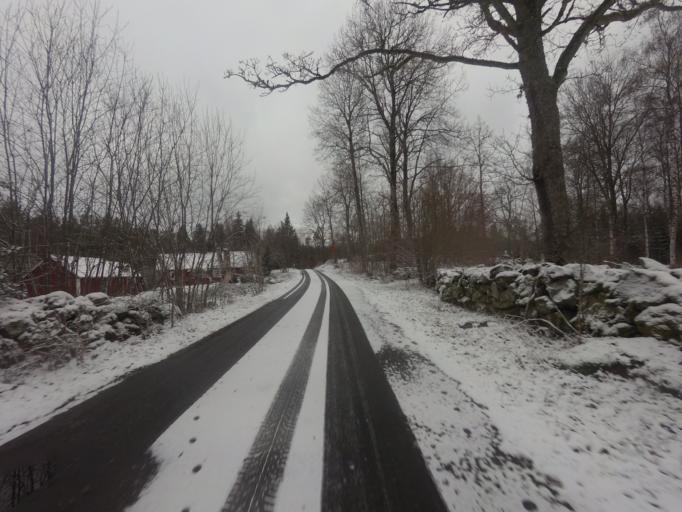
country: SE
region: Skane
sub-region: Osby Kommun
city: Lonsboda
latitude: 56.3936
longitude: 14.2895
